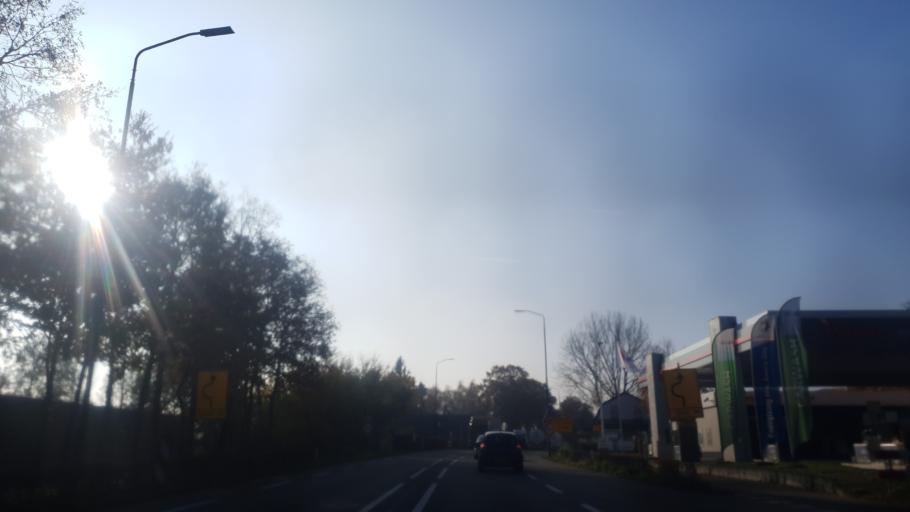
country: NL
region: North Brabant
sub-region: Gemeente Grave
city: Grave
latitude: 51.7516
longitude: 5.7326
